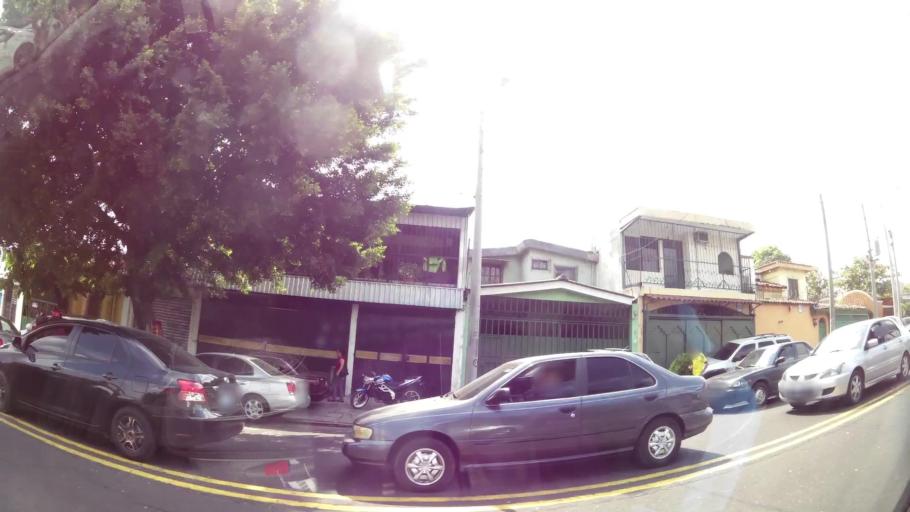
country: SV
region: San Salvador
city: Mejicanos
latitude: 13.7104
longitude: -89.2333
